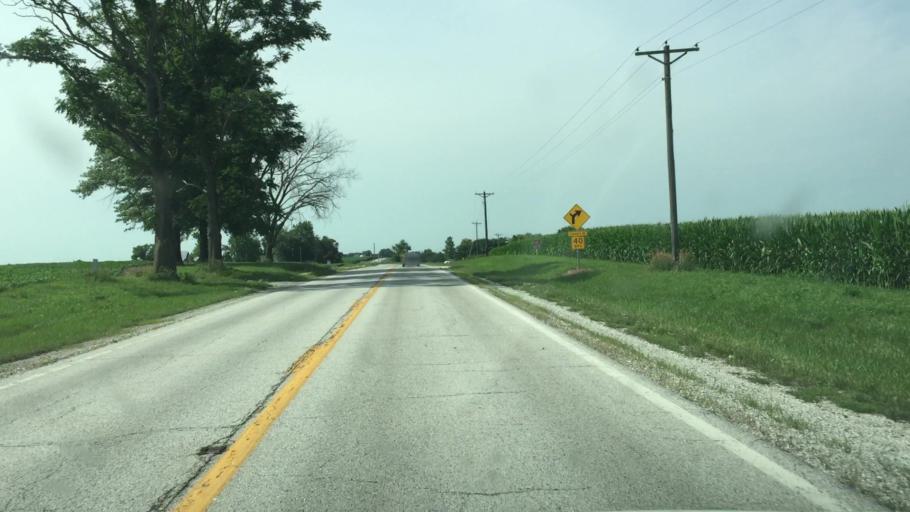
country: US
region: Iowa
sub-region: Lee County
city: Fort Madison
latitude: 40.5548
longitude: -91.3077
